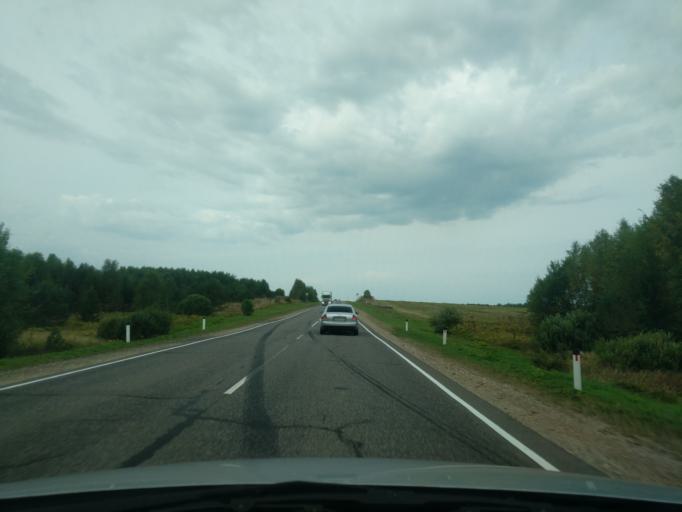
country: RU
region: Kirov
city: Mirnyy
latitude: 58.2730
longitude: 47.7780
